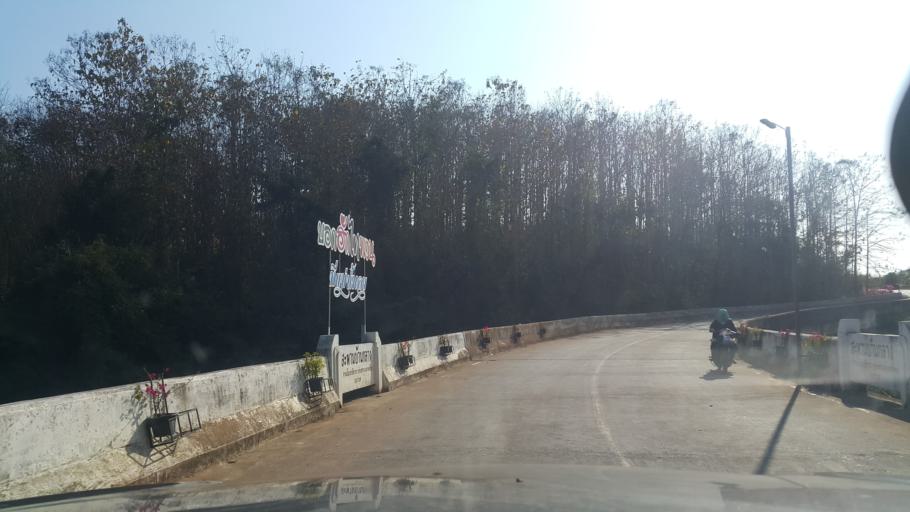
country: TH
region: Loei
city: Chiang Khan
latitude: 17.8035
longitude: 101.6264
